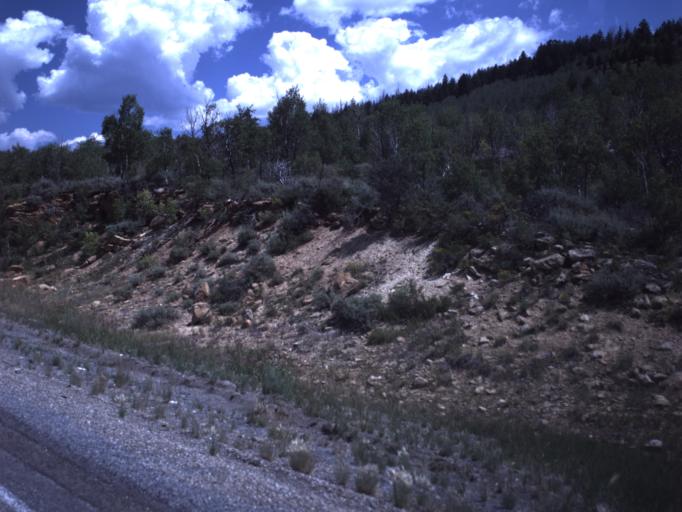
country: US
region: Utah
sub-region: Carbon County
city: Helper
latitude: 39.8500
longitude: -111.1277
